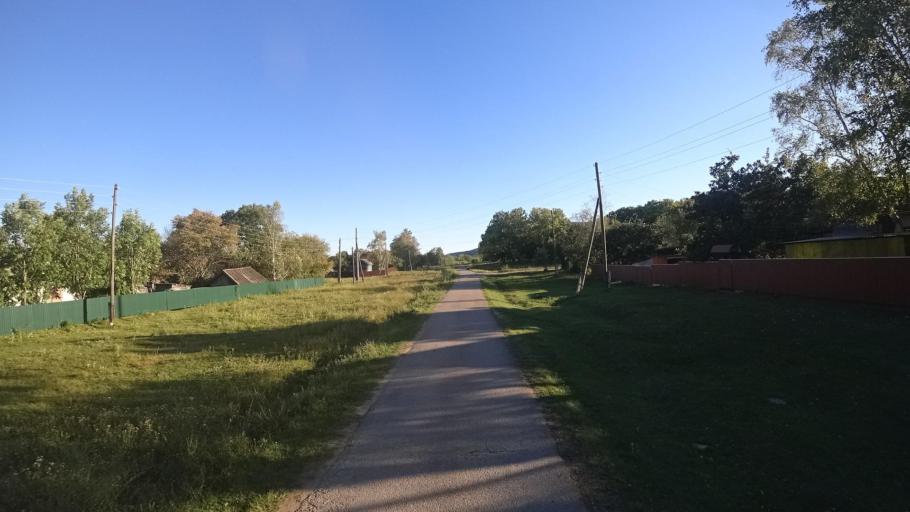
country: RU
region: Primorskiy
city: Kirovskiy
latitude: 44.8299
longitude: 133.5752
